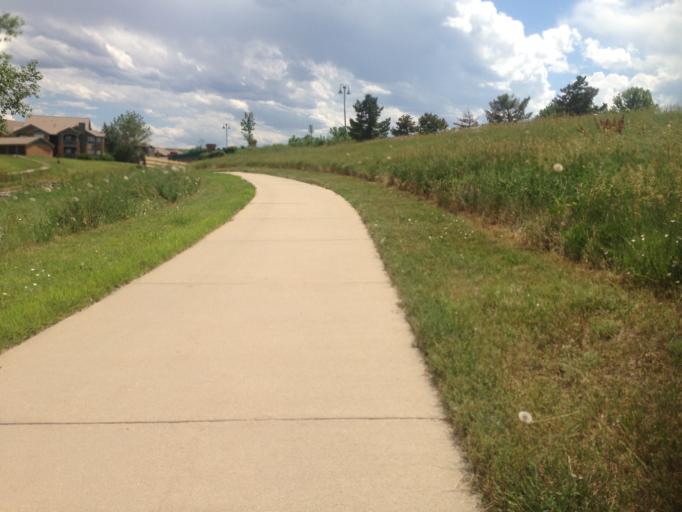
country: US
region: Colorado
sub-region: Boulder County
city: Superior
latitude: 39.9346
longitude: -105.1452
